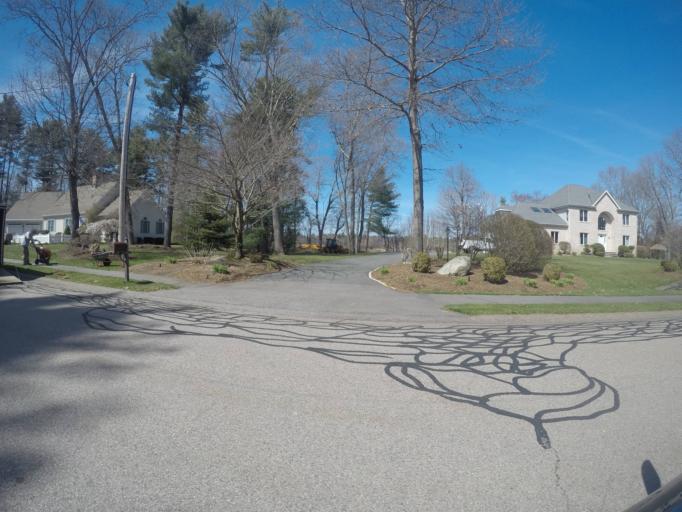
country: US
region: Massachusetts
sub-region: Bristol County
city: Easton
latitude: 42.0305
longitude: -71.0836
